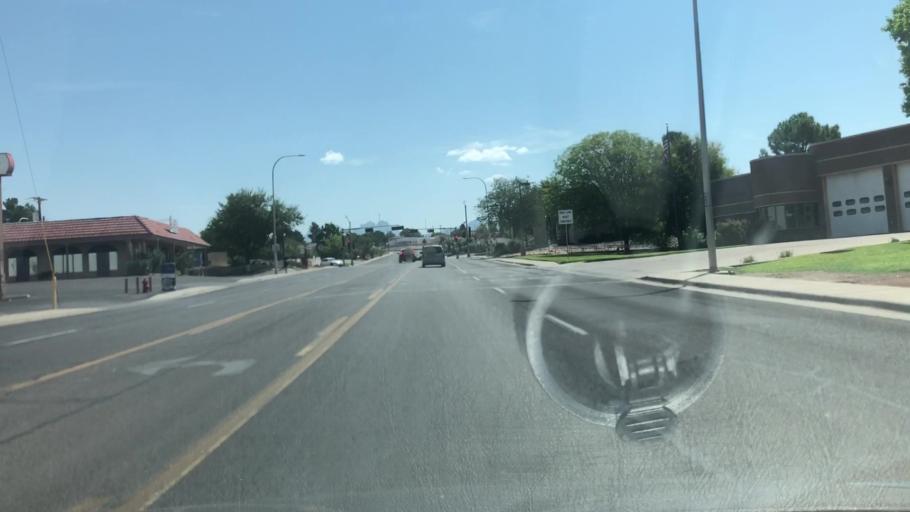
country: US
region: New Mexico
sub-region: Dona Ana County
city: University Park
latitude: 32.2996
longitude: -106.7382
